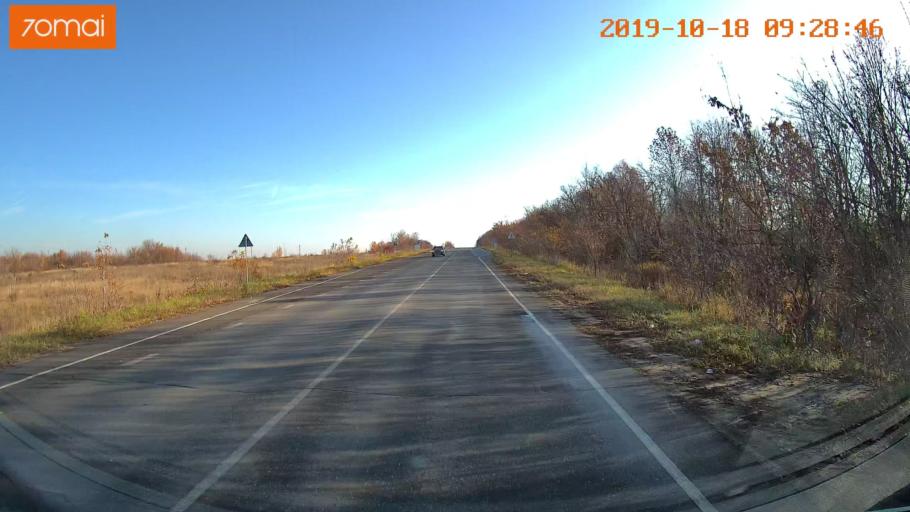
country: RU
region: Tula
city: Yefremov
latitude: 53.1343
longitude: 38.1426
